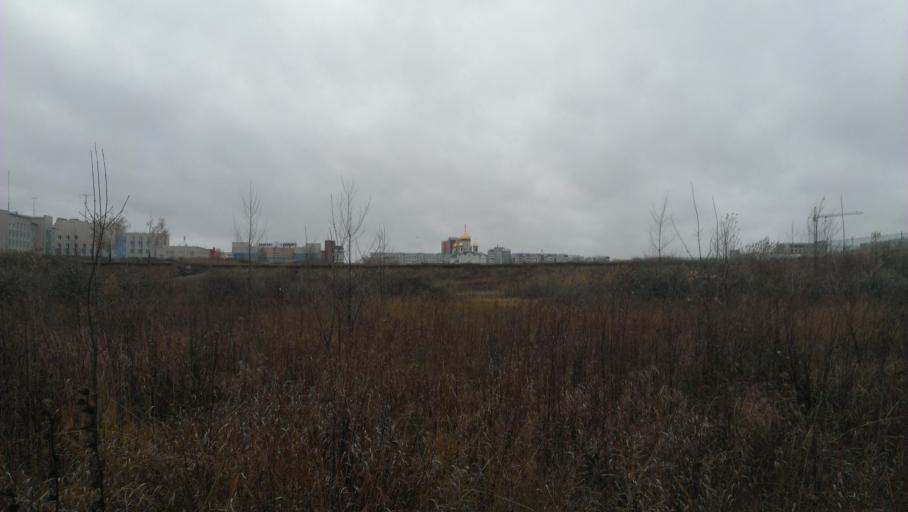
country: RU
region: Altai Krai
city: Novosilikatnyy
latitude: 53.3413
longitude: 83.6848
